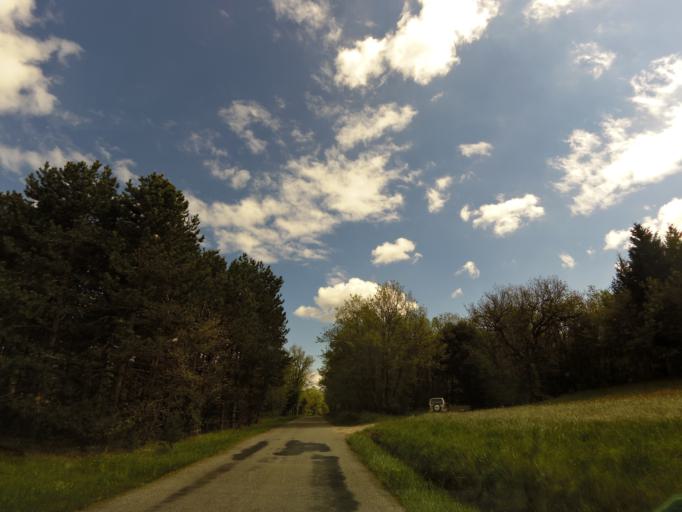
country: FR
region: Languedoc-Roussillon
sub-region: Departement de l'Aude
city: Saint-Martin-Lalande
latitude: 43.3463
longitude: 2.0612
